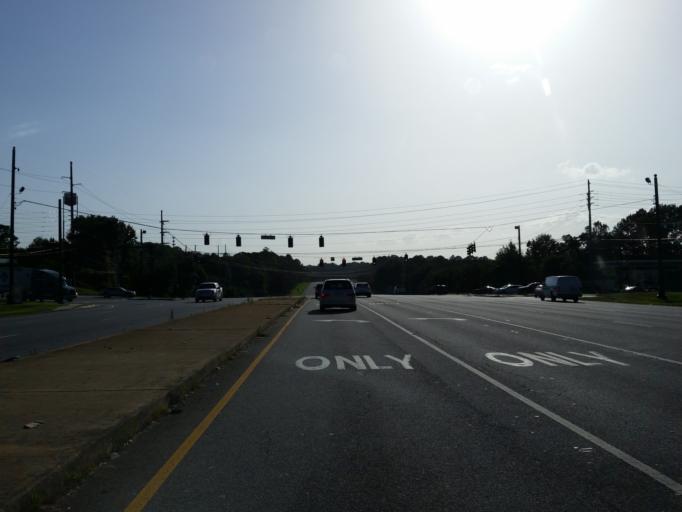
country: US
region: Georgia
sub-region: Cobb County
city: Smyrna
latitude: 33.9228
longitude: -84.4909
